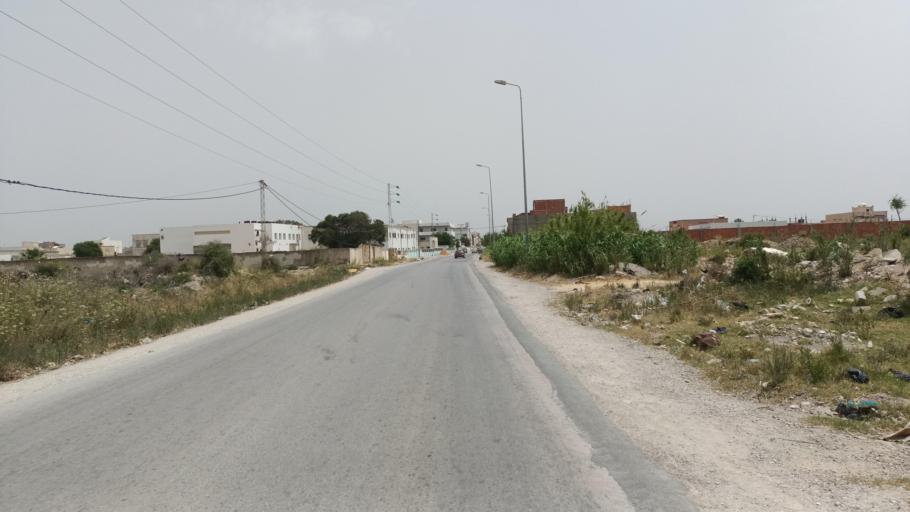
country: TN
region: Nabul
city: Manzil Bu Zalafah
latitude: 36.7089
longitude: 10.4837
